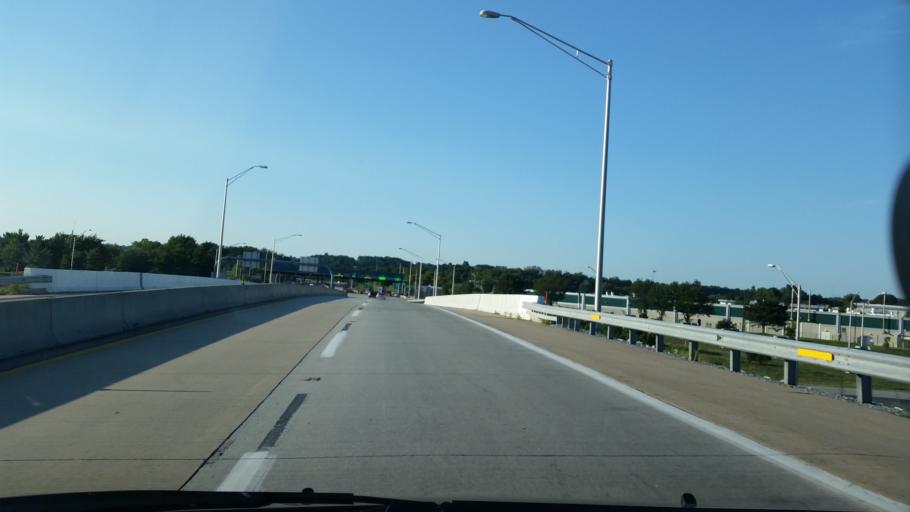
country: US
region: Pennsylvania
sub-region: Dauphin County
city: Highspire
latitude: 40.2139
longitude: -76.7861
